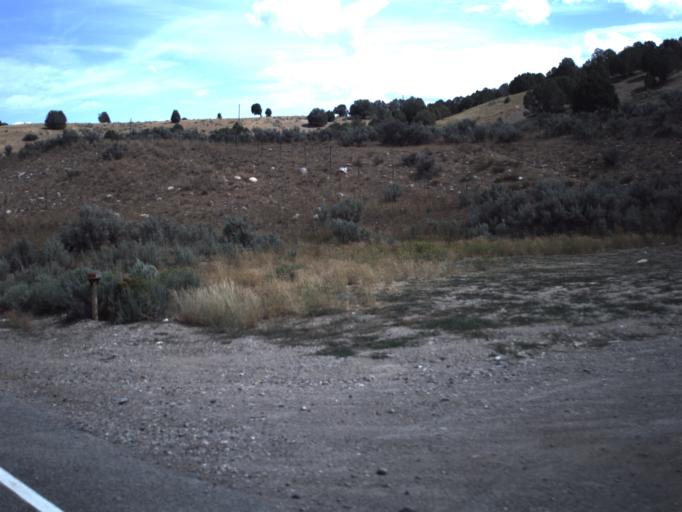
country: US
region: Utah
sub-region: Utah County
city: Woodland Hills
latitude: 39.9440
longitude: -111.5403
